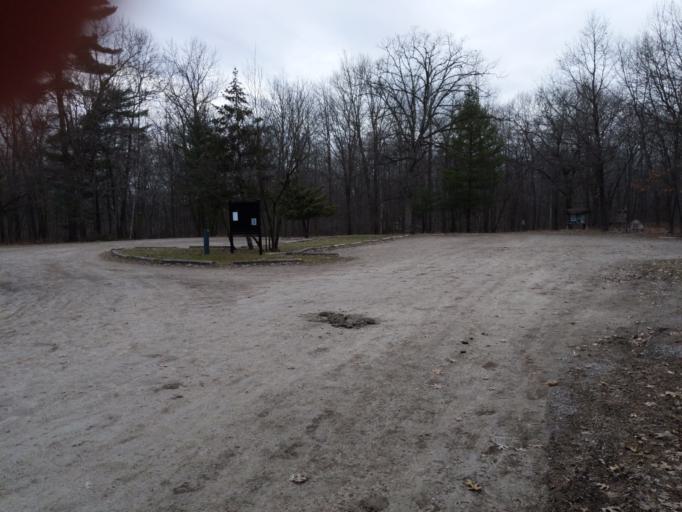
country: US
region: Michigan
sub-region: Bay County
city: Bay City
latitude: 43.6752
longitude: -83.9225
